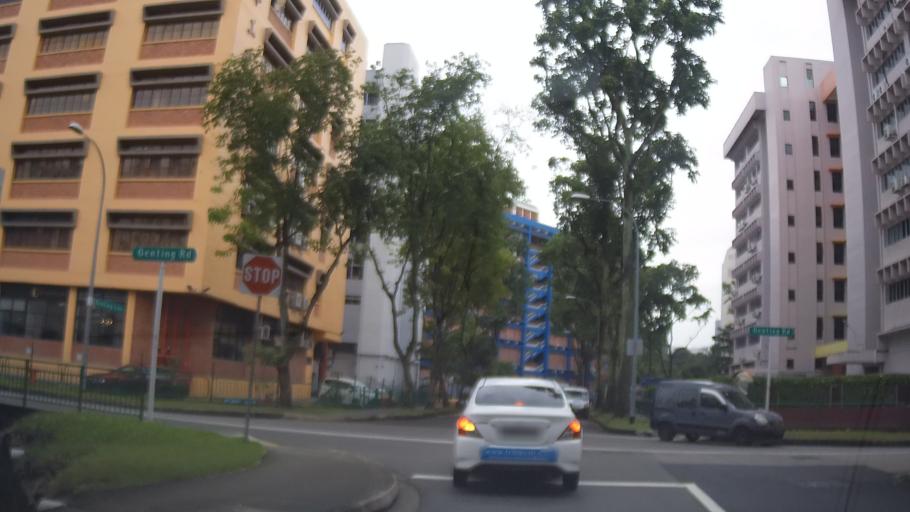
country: SG
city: Singapore
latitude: 1.3291
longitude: 103.8745
